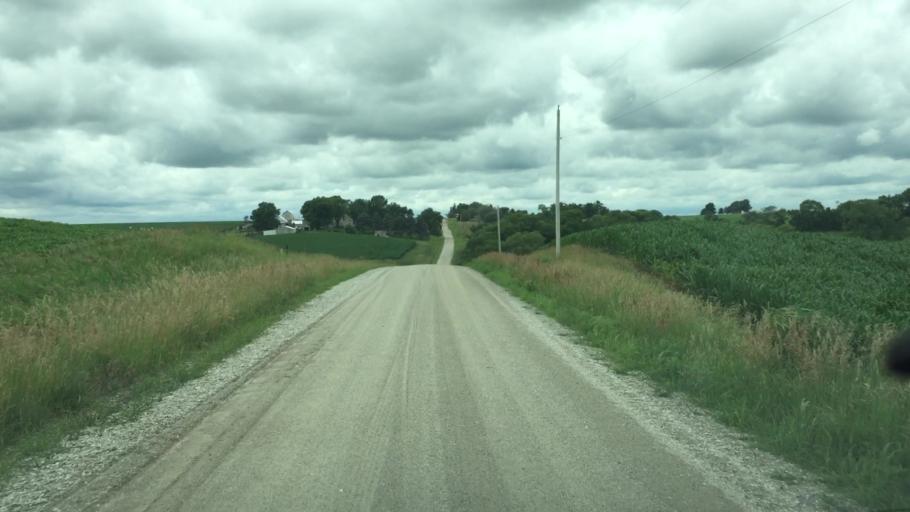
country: US
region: Iowa
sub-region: Jasper County
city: Monroe
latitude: 41.6009
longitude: -93.1398
